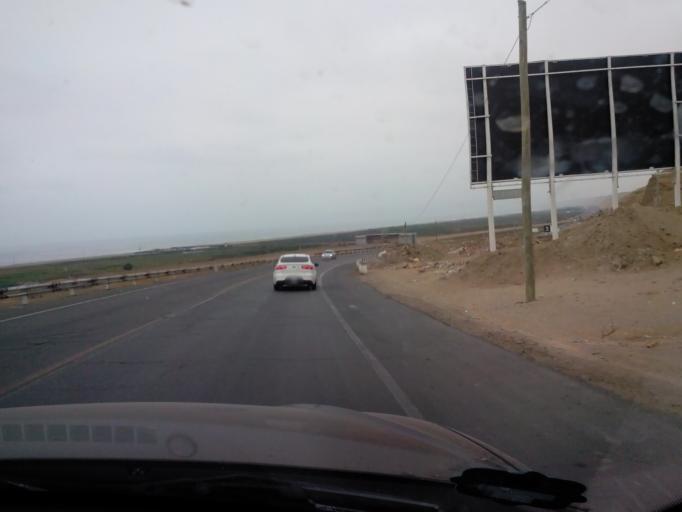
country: PE
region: Ica
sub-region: Provincia de Chincha
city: Sunampe
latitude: -13.4136
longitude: -76.1883
